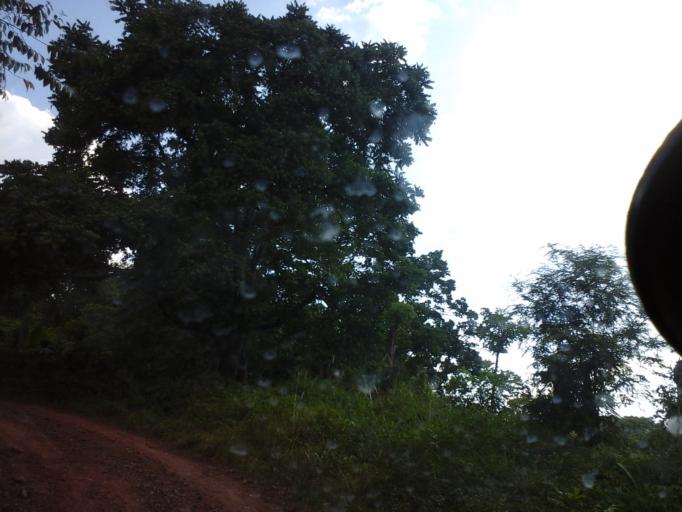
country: CO
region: Cesar
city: San Diego
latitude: 10.2514
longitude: -73.1125
